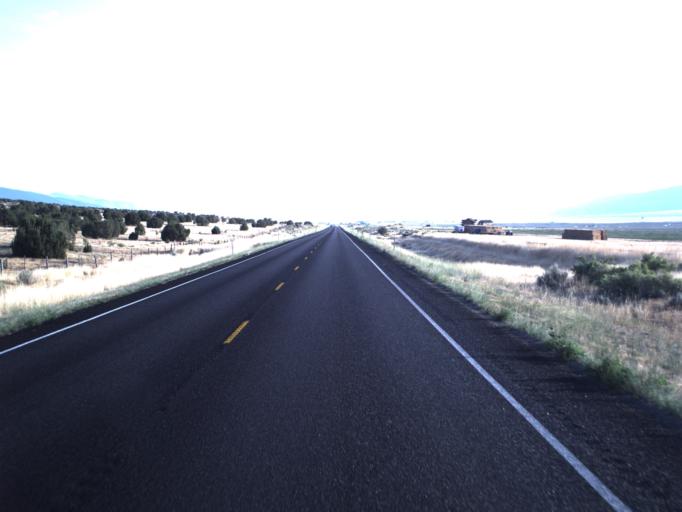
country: US
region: Utah
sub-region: Sanpete County
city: Moroni
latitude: 39.4667
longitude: -111.5331
